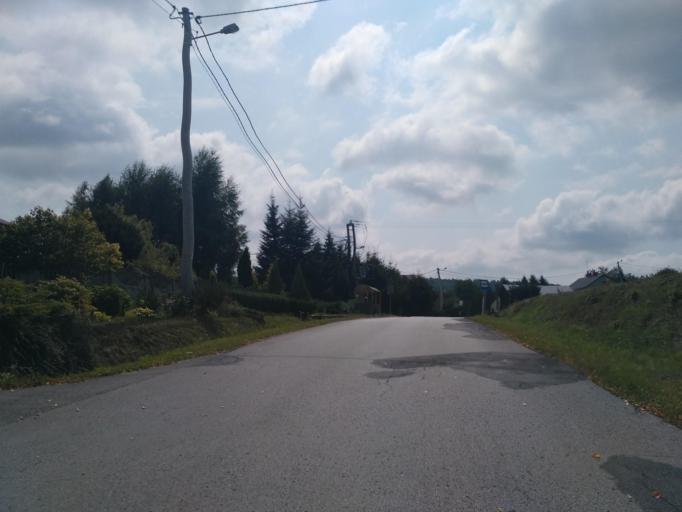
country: PL
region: Subcarpathian Voivodeship
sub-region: Powiat lancucki
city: Kraczkowa
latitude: 50.0190
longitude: 22.1776
